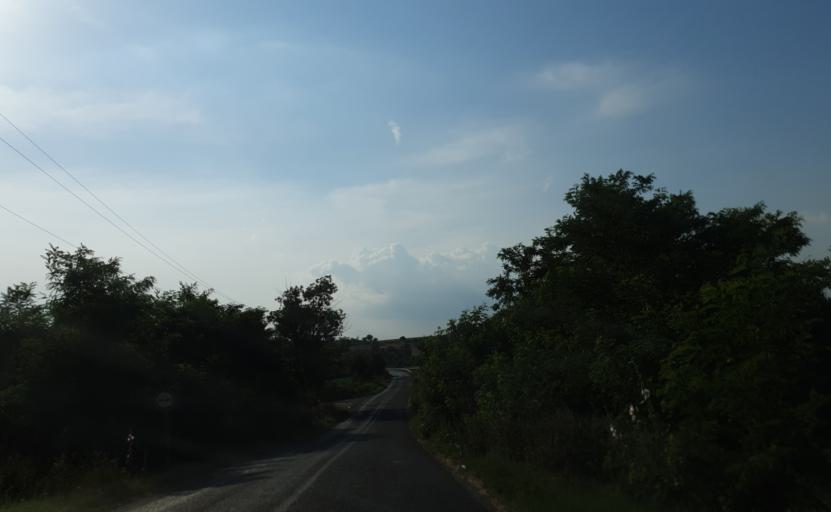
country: TR
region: Tekirdag
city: Muratli
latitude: 41.1945
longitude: 27.4737
